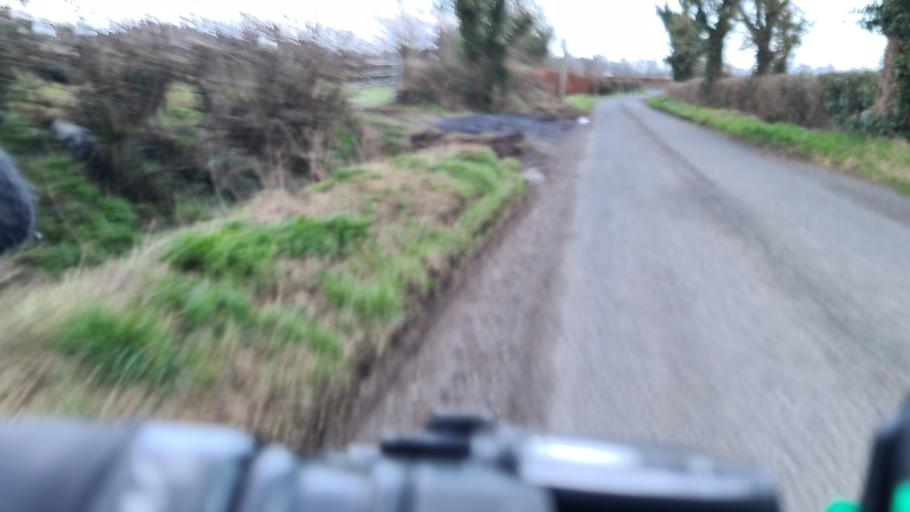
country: IE
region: Leinster
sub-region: Kildare
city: Maynooth
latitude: 53.3396
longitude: -6.5973
